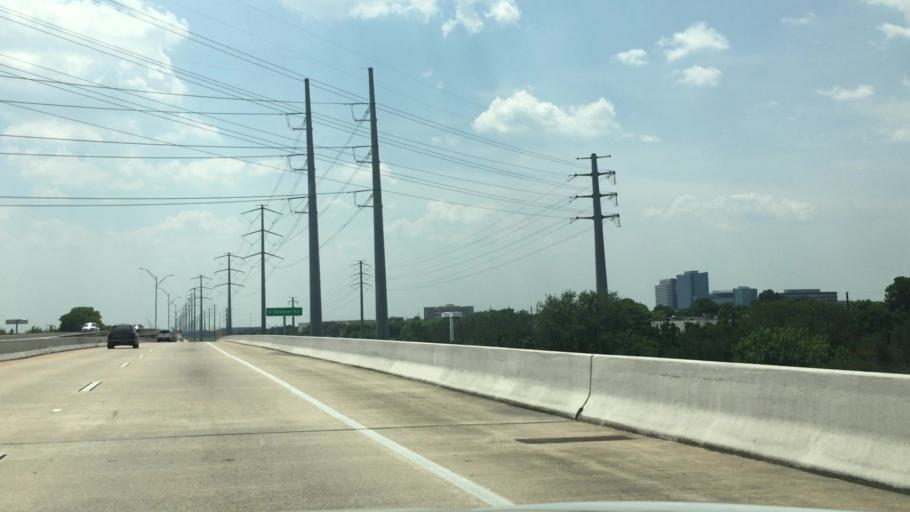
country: US
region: Texas
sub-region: Harris County
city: Piney Point Village
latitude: 29.7199
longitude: -95.5381
